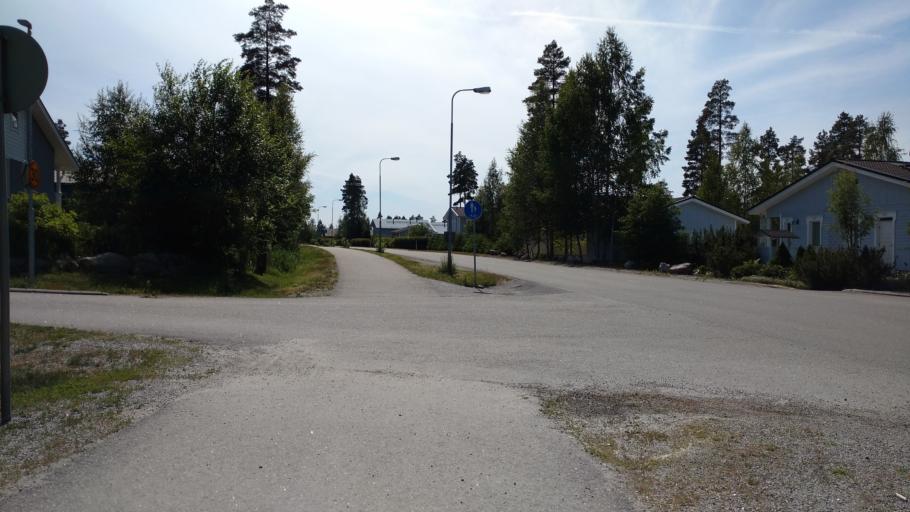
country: FI
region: Varsinais-Suomi
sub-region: Salo
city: Salo
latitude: 60.4044
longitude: 23.1900
